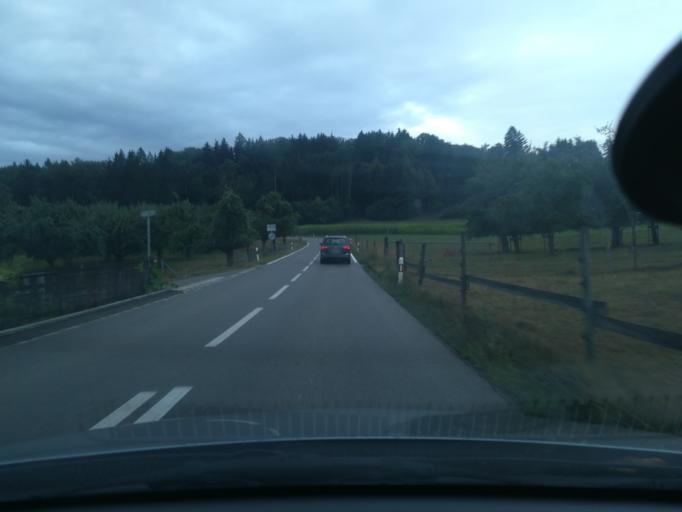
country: CH
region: Thurgau
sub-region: Frauenfeld District
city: Huttwilen
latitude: 47.6257
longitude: 8.8789
